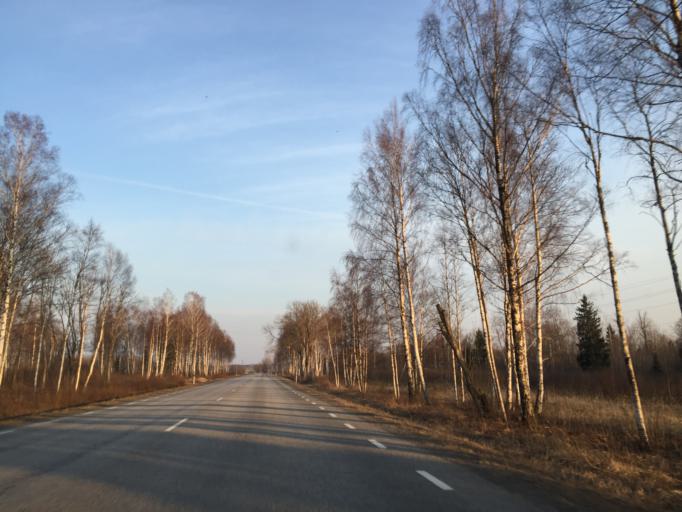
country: EE
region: Laeaene
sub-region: Lihula vald
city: Lihula
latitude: 58.5423
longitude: 24.0054
